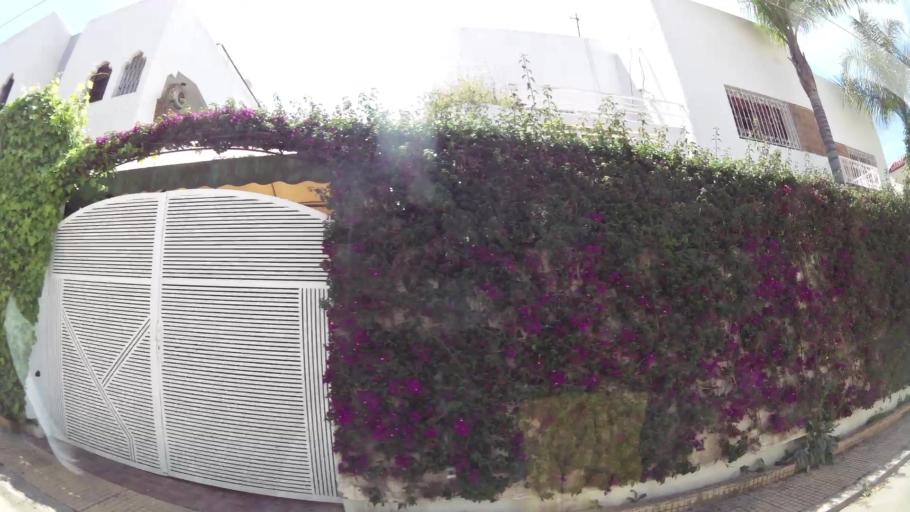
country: MA
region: Fes-Boulemane
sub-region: Fes
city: Fes
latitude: 34.0154
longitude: -4.9934
